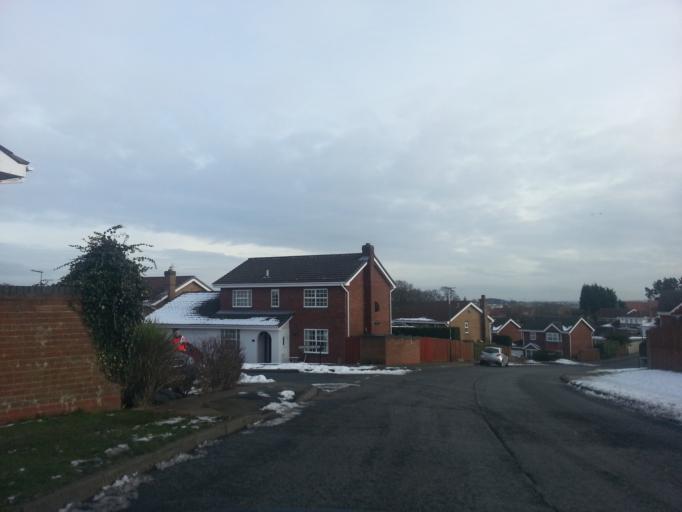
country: GB
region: England
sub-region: County Durham
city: Crook
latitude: 54.7115
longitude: -1.7661
